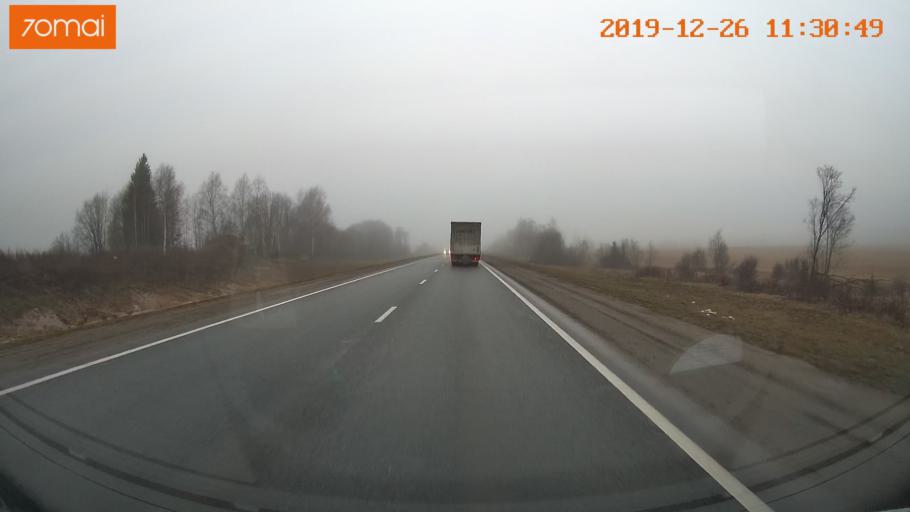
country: RU
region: Vologda
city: Chebsara
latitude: 59.1667
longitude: 38.7657
